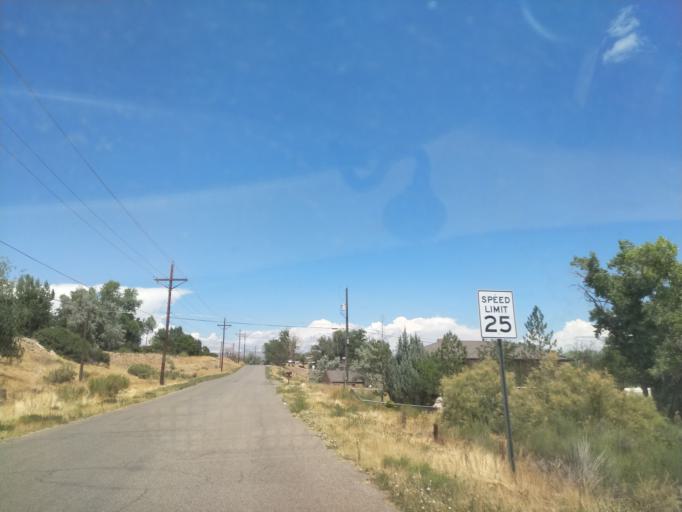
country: US
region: Colorado
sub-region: Mesa County
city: Redlands
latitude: 39.0740
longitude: -108.6403
